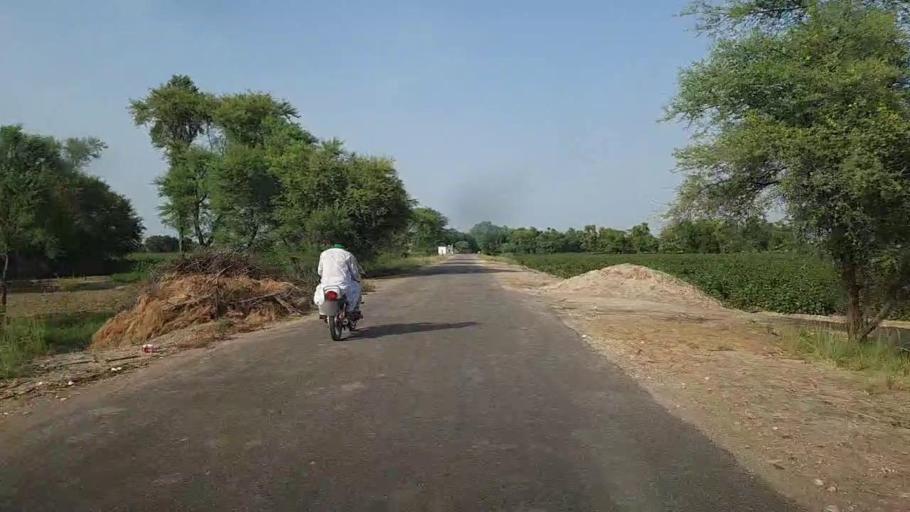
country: PK
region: Sindh
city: Ubauro
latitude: 28.0845
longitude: 69.8388
